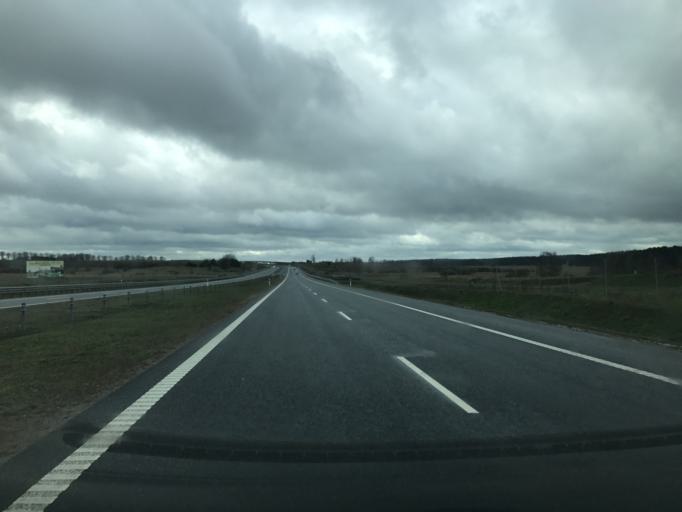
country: PL
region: Warmian-Masurian Voivodeship
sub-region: Powiat olsztynski
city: Olsztynek
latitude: 53.6023
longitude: 20.2910
